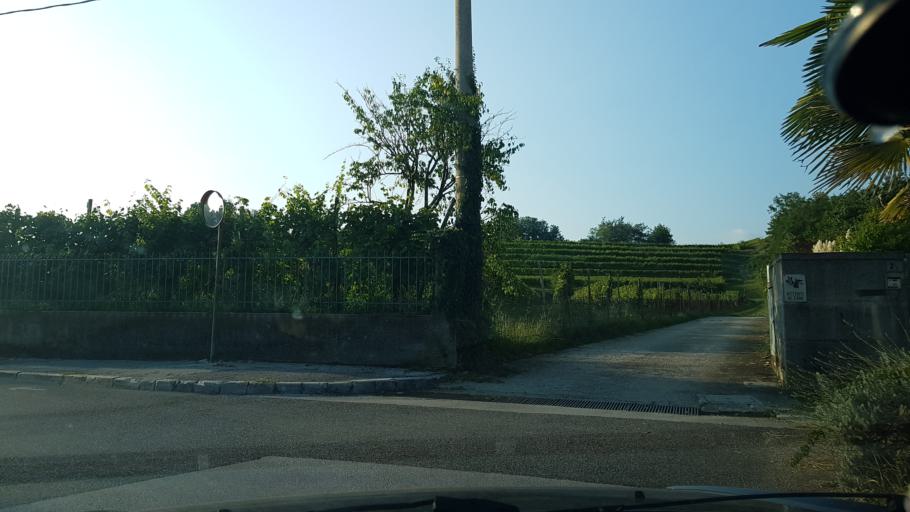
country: IT
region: Friuli Venezia Giulia
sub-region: Provincia di Gorizia
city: Mossa
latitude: 45.9397
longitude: 13.5793
